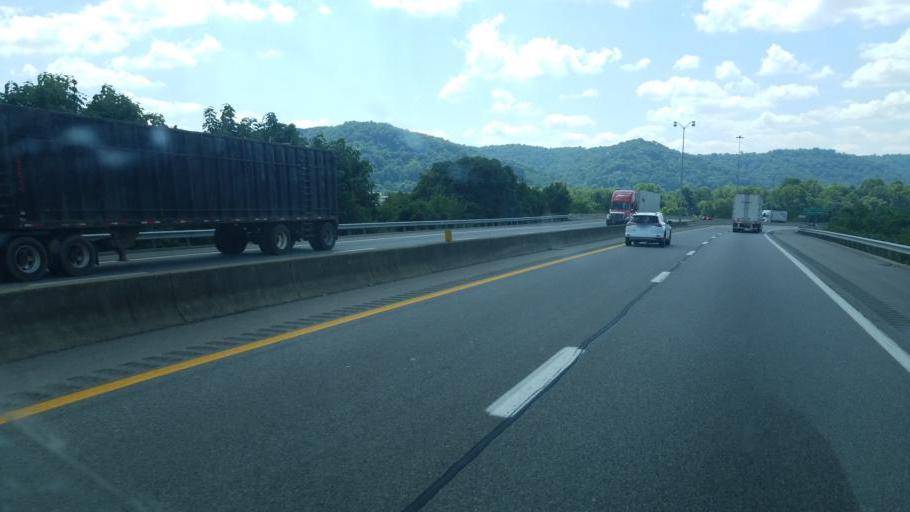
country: US
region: West Virginia
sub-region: Kanawha County
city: Rand
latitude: 38.3175
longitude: -81.5591
